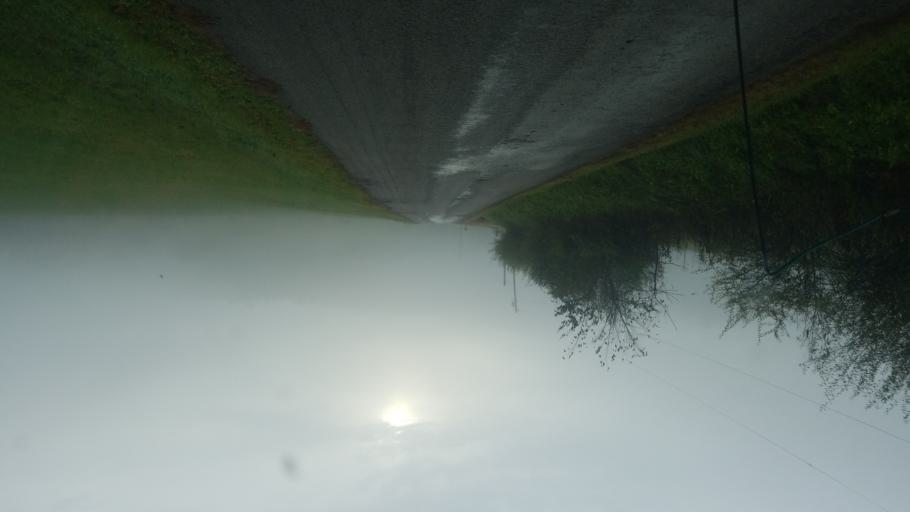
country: US
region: Ohio
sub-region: Athens County
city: Glouster
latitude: 39.4497
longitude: -81.9242
